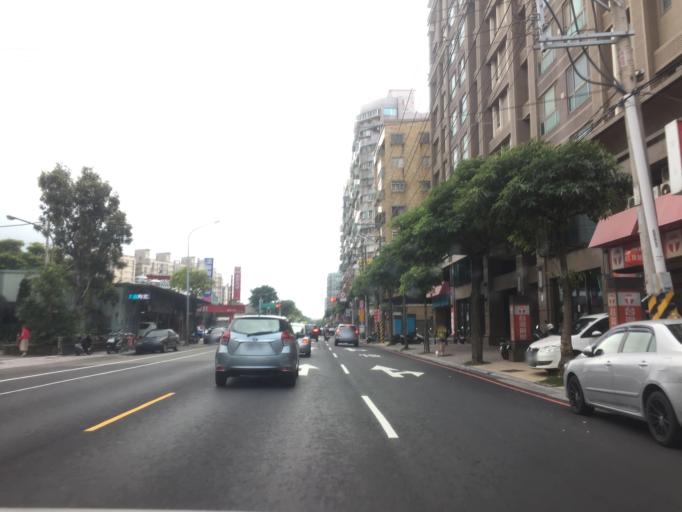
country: TW
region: Taiwan
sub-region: Taoyuan
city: Taoyuan
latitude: 24.9641
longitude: 121.3068
